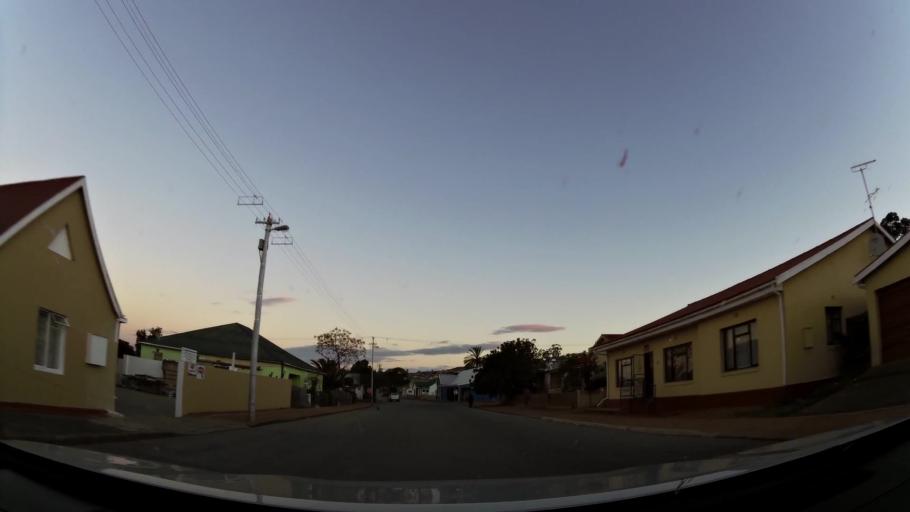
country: ZA
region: Western Cape
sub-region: Eden District Municipality
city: Riversdale
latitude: -34.0946
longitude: 21.2614
